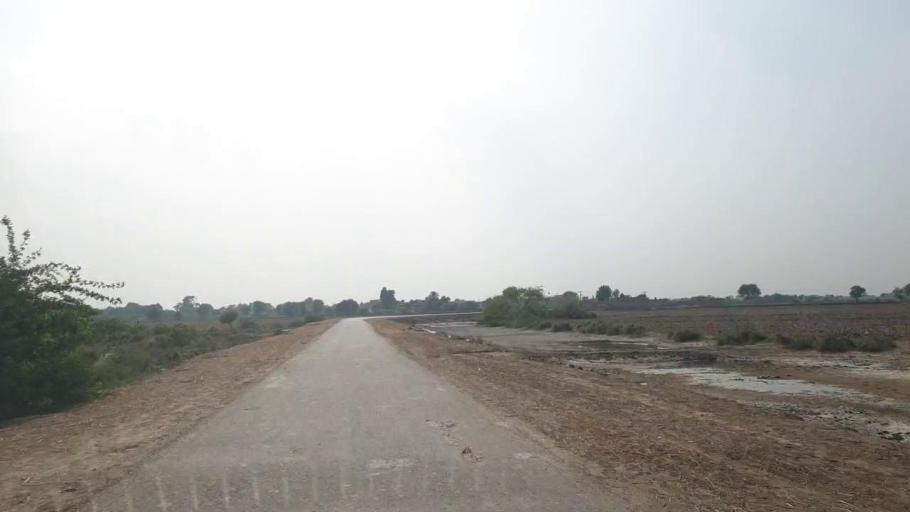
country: PK
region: Sindh
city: Rajo Khanani
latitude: 25.0461
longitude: 68.8082
